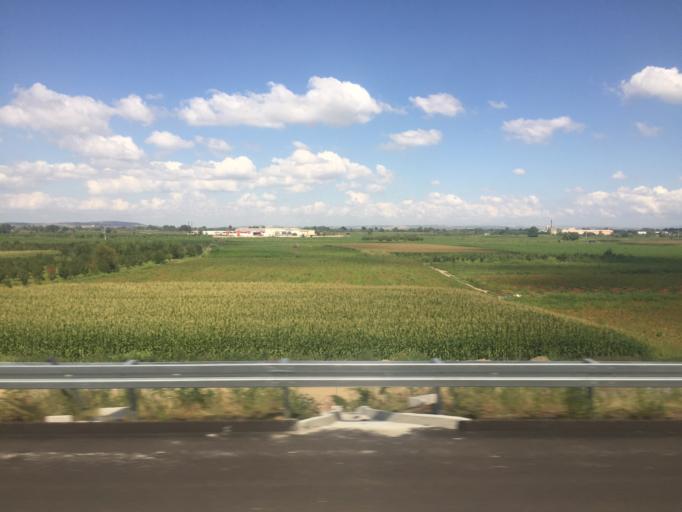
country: TR
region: Balikesir
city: Gobel
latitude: 40.0643
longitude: 28.2449
